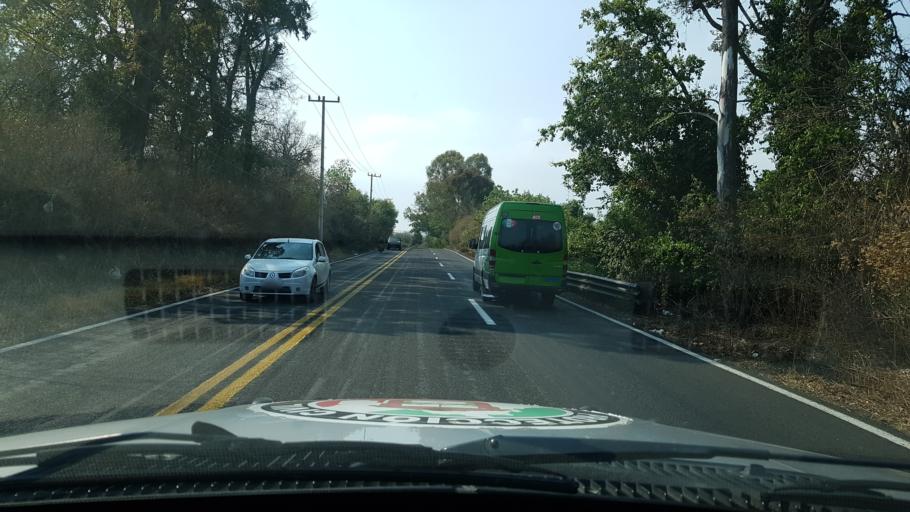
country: MX
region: Mexico
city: Tepetlixpa
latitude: 19.0068
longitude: -98.8219
